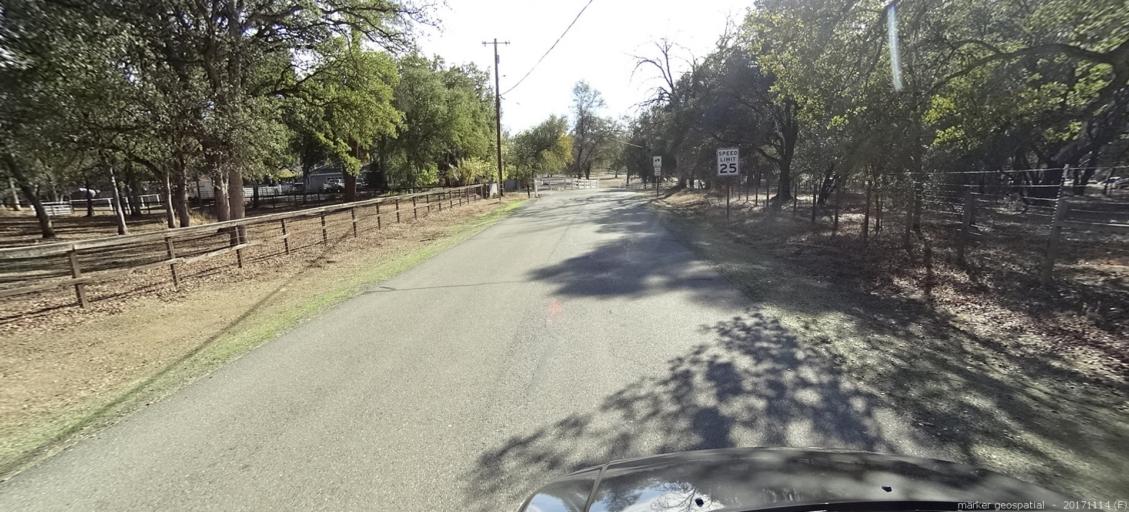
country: US
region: California
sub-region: Shasta County
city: Anderson
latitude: 40.3833
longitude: -122.4518
